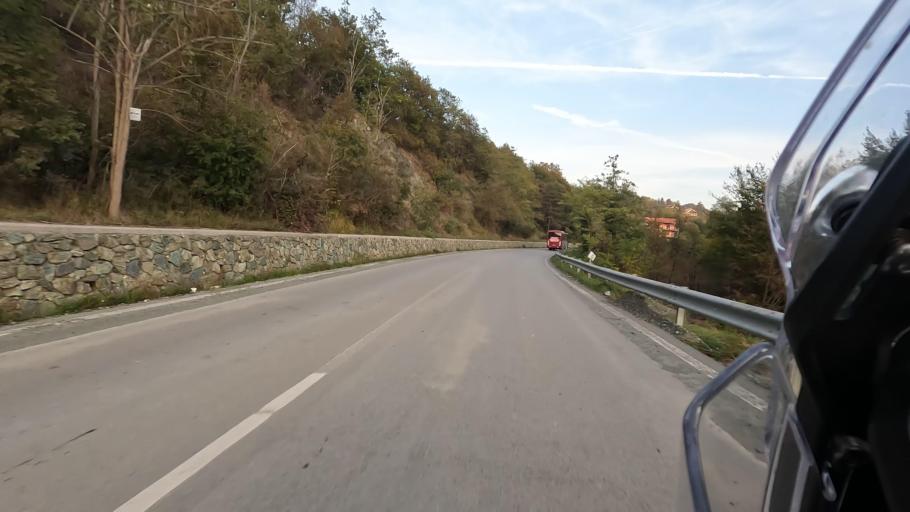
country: IT
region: Liguria
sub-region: Provincia di Savona
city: Pontinvrea
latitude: 44.4387
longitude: 8.4425
